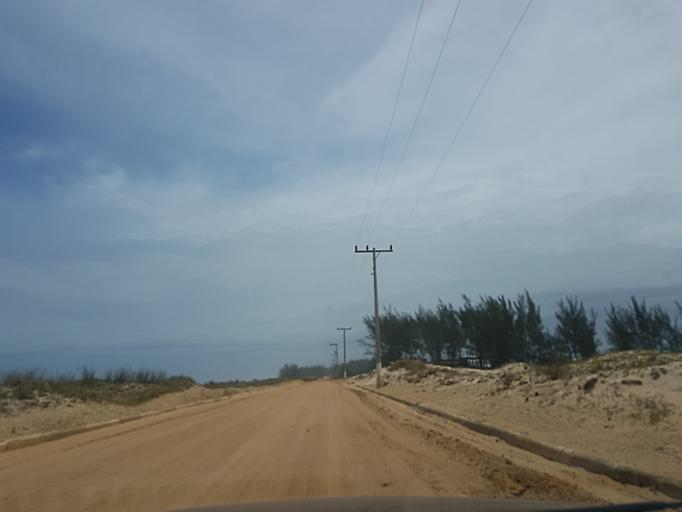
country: BR
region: Santa Catarina
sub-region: Jaguaruna
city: Jaguaruna
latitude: -28.6679
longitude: -48.9695
